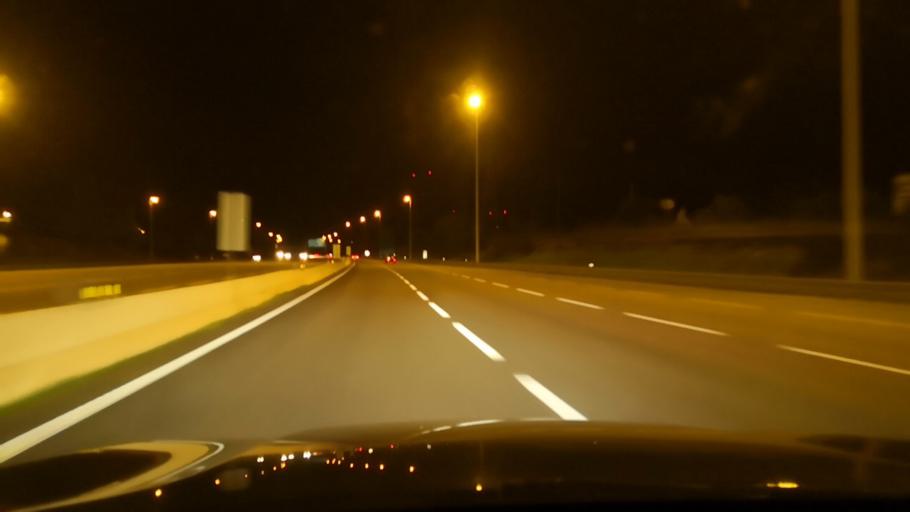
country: PT
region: Setubal
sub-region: Palmela
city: Palmela
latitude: 38.5693
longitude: -8.8662
